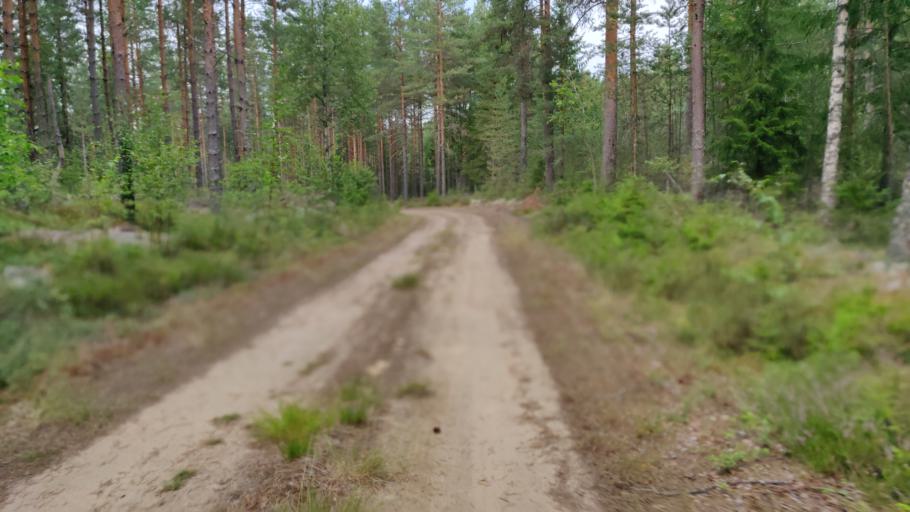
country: SE
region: Vaermland
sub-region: Hagfors Kommun
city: Hagfors
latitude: 60.0165
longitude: 13.5584
